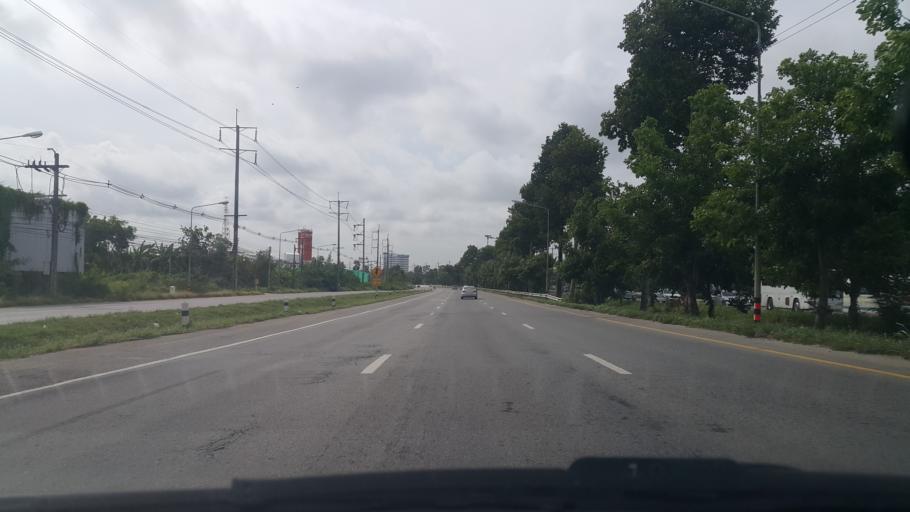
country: TH
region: Rayong
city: Rayong
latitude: 12.6860
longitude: 101.2982
